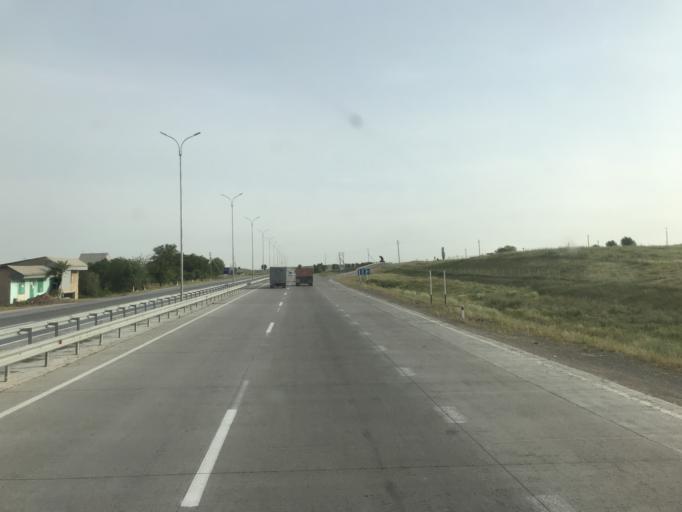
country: UZ
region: Toshkent
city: Qibray
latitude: 41.5638
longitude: 69.4084
